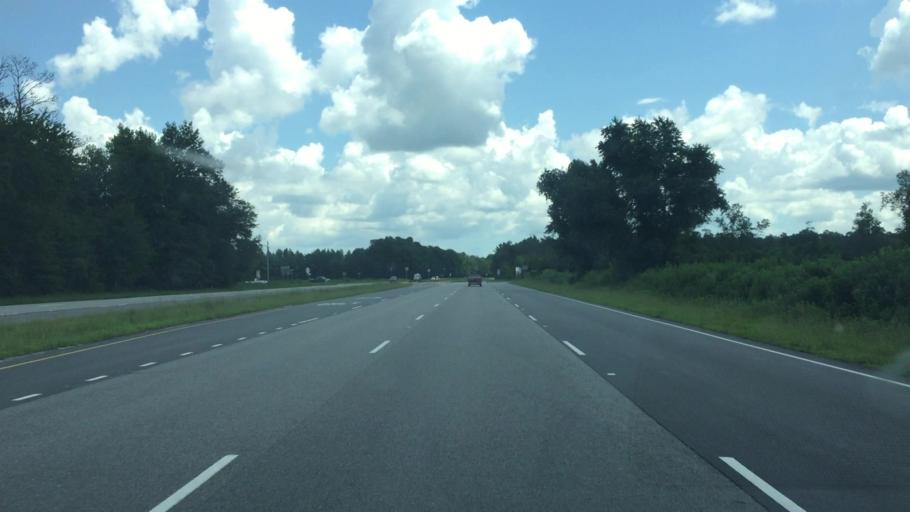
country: US
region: South Carolina
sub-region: Horry County
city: Loris
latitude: 34.0354
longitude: -78.8112
